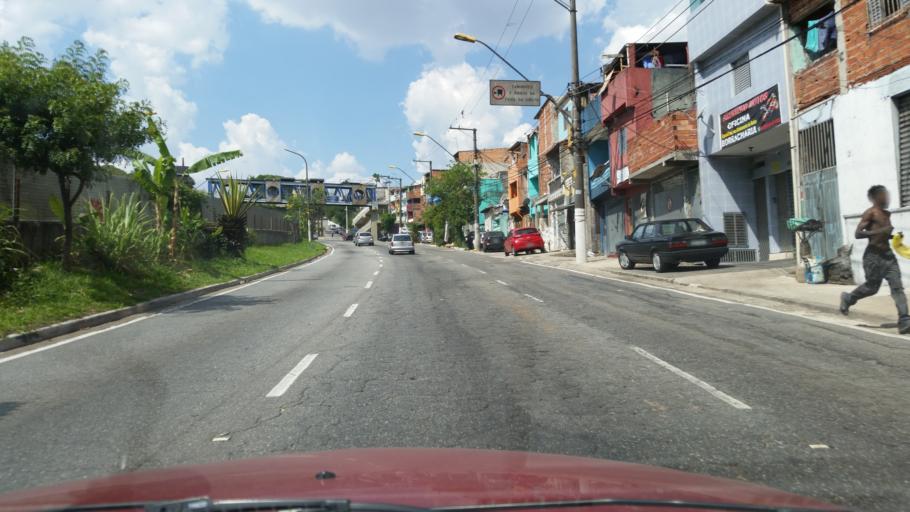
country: BR
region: Sao Paulo
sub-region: Santo Andre
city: Santo Andre
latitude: -23.6574
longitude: -46.5502
